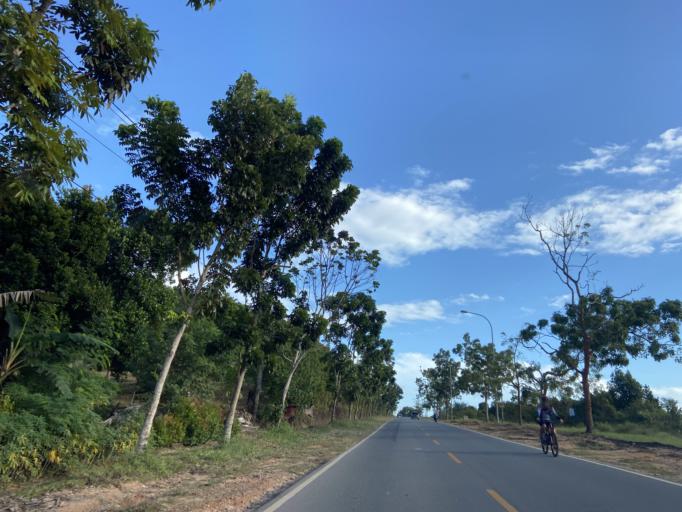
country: SG
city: Singapore
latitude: 0.9938
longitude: 104.0338
